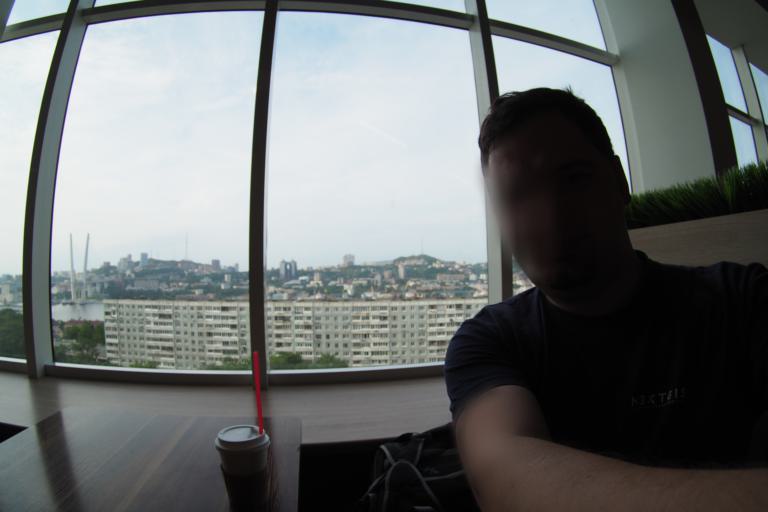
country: RU
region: Primorskiy
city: Vladivostok
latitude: 43.1005
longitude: 131.9033
